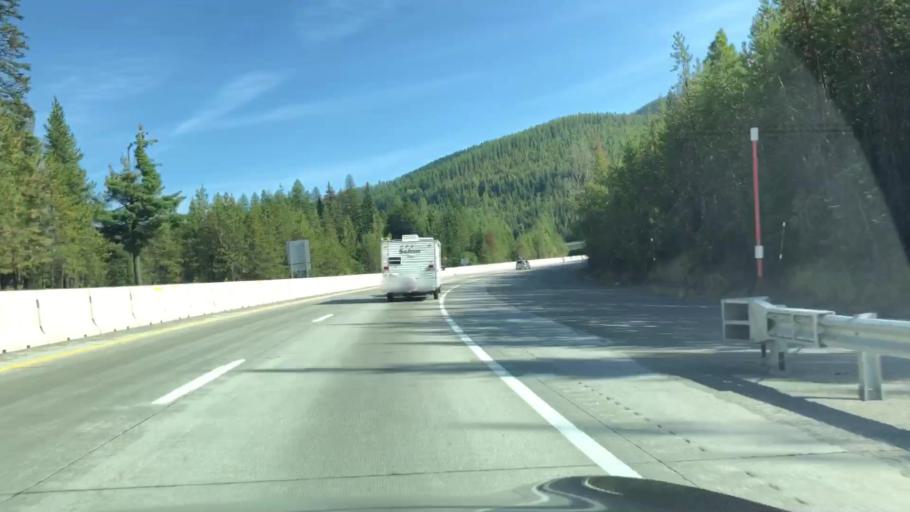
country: US
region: Idaho
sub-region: Shoshone County
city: Wallace
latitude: 47.4691
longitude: -115.7615
